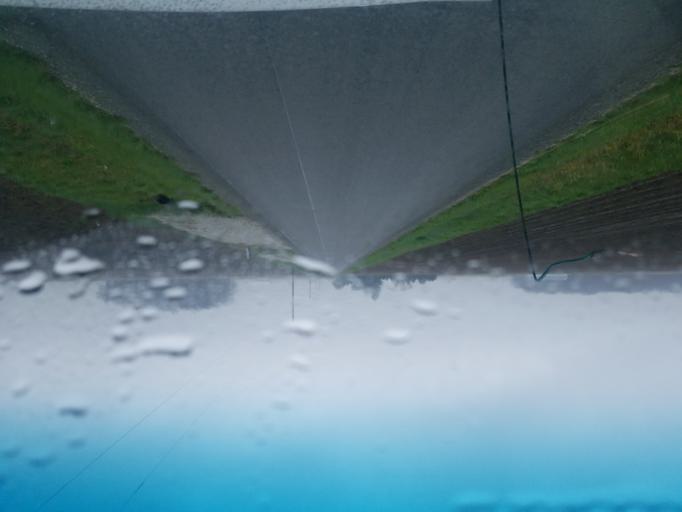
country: US
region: Ohio
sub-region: Wyandot County
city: Carey
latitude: 40.9923
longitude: -83.3533
